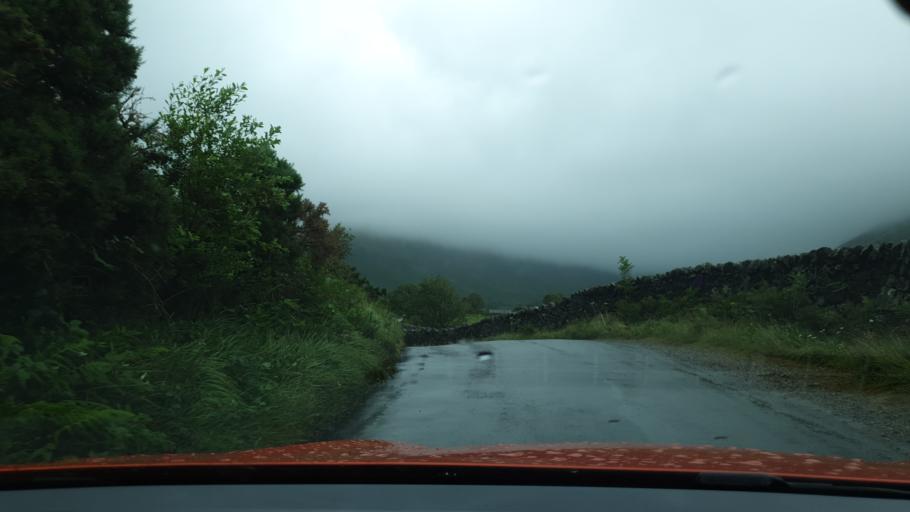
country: GB
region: England
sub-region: Cumbria
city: Keswick
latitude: 54.4588
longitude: -3.2637
